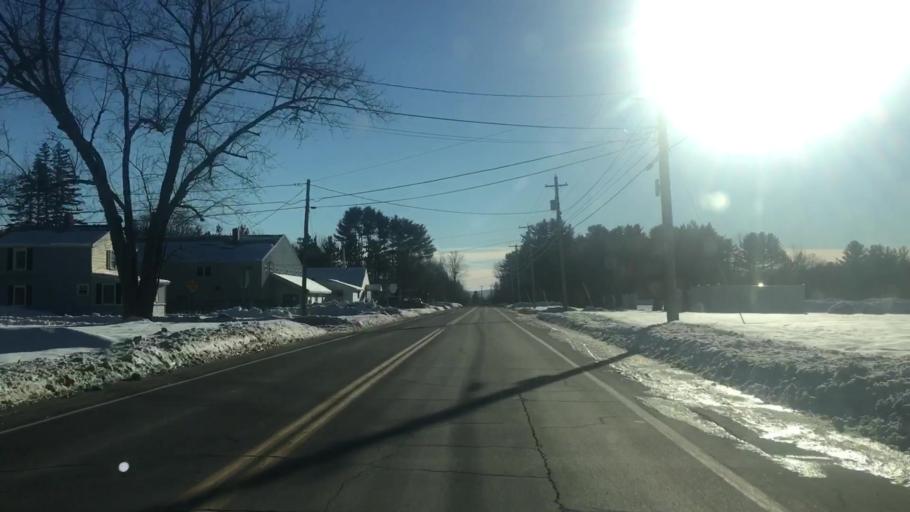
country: US
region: Maine
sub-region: Somerset County
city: Madison
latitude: 44.7866
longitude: -69.8835
